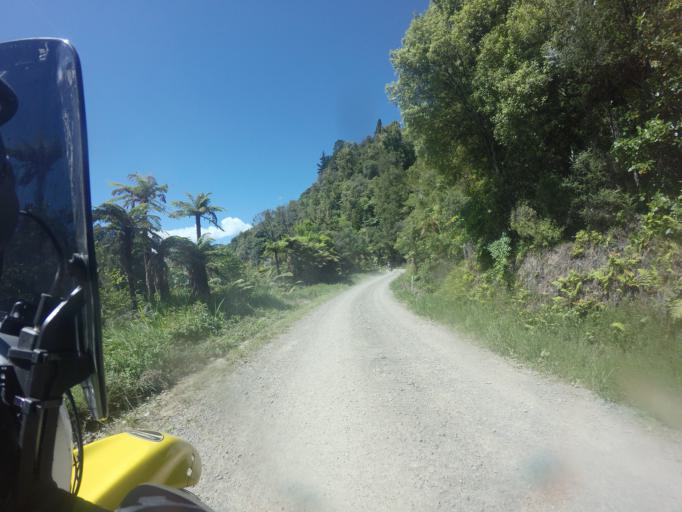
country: NZ
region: Bay of Plenty
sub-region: Opotiki District
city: Opotiki
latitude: -38.2968
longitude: 177.3372
